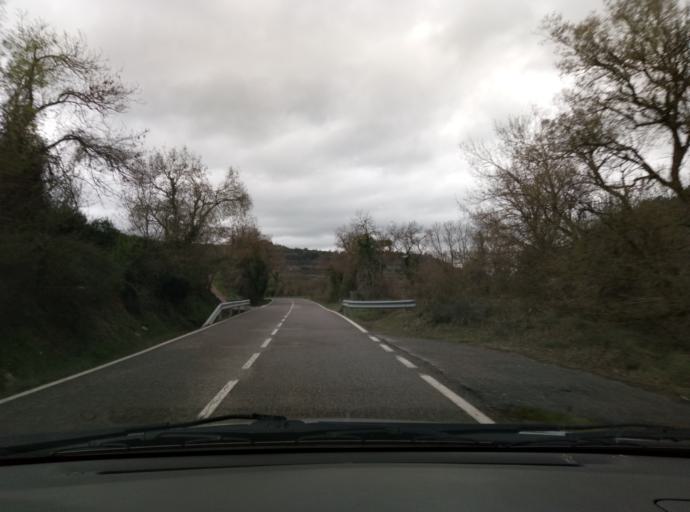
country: ES
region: Catalonia
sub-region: Provincia de Tarragona
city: Vallfogona de Riucorb
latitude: 41.5613
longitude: 1.2263
